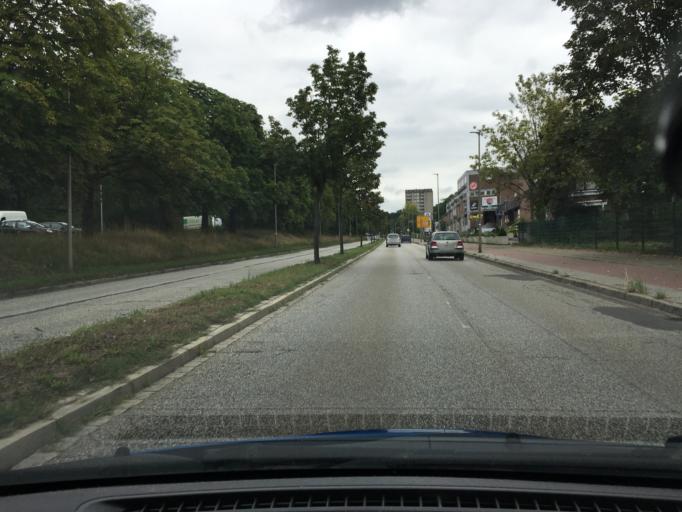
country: DE
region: Schleswig-Holstein
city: Geesthacht
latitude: 53.4359
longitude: 10.3794
